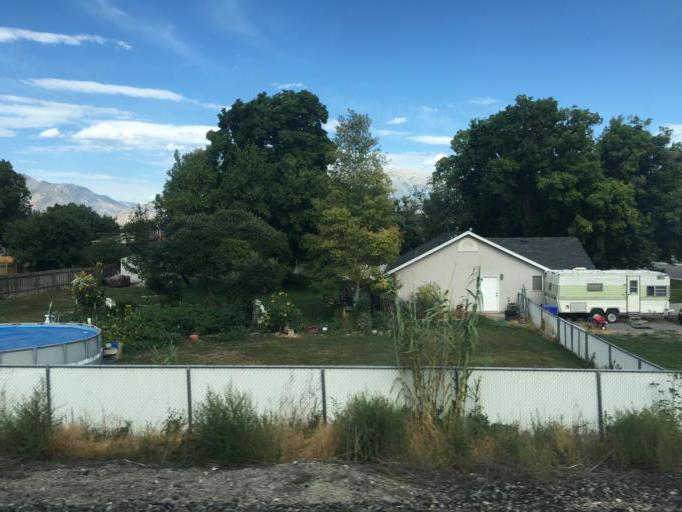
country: US
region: Utah
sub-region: Utah County
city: Lehi
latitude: 40.3846
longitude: -111.8552
